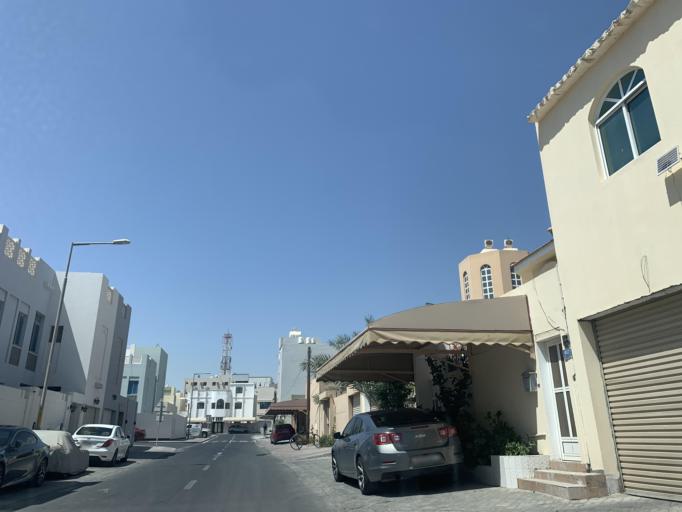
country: BH
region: Northern
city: Ar Rifa'
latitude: 26.1325
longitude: 50.5805
